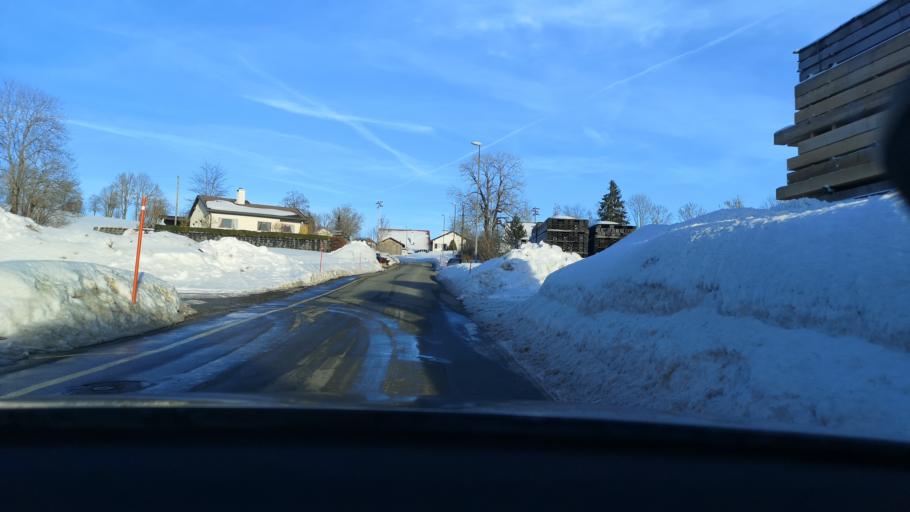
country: CH
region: Neuchatel
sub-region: Val-de-Travers District
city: Fleurier
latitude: 46.9173
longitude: 6.5219
